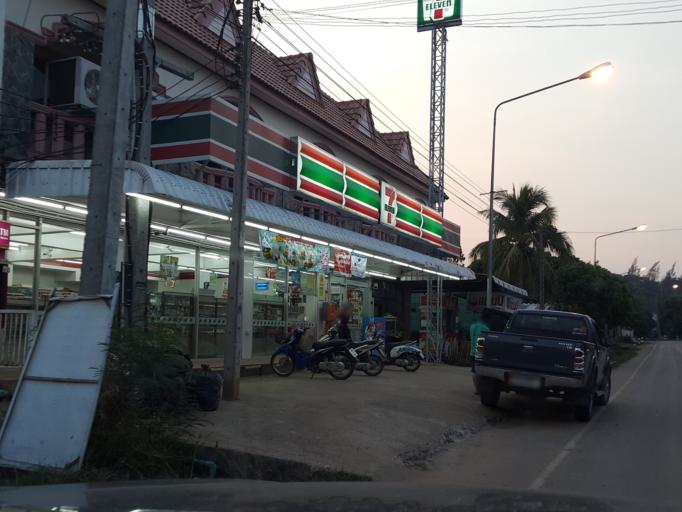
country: TH
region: Lamphun
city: Thung Hua Chang
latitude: 18.0000
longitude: 99.0303
